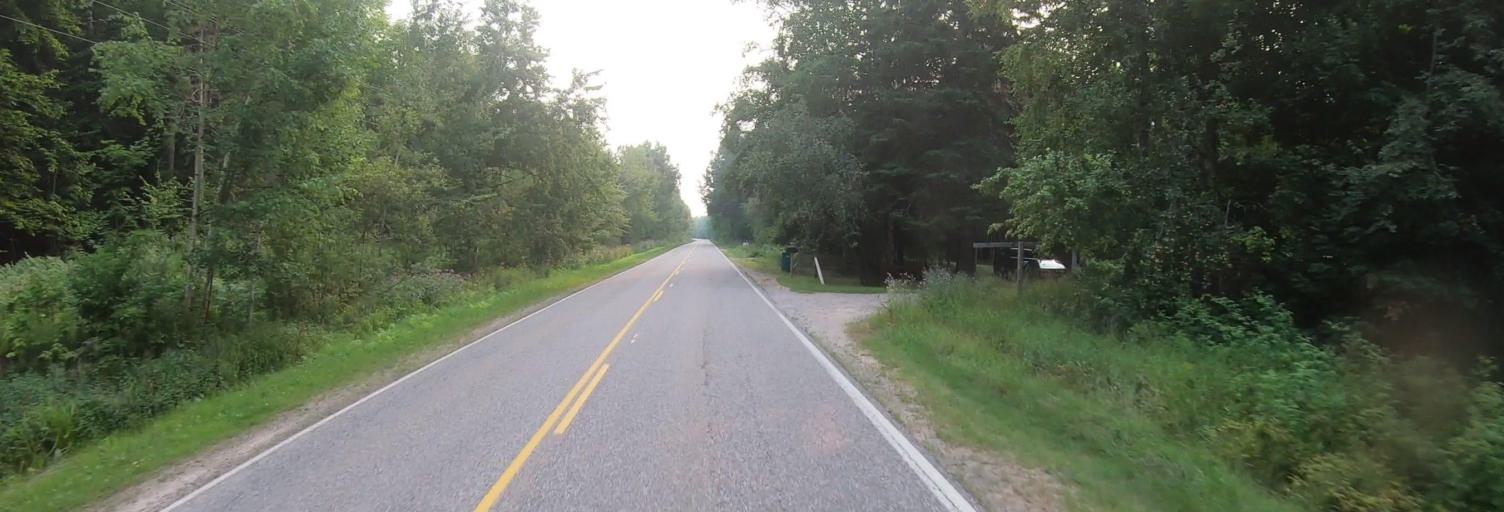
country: US
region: Michigan
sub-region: Chippewa County
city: Sault Ste. Marie
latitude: 46.4650
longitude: -84.7287
